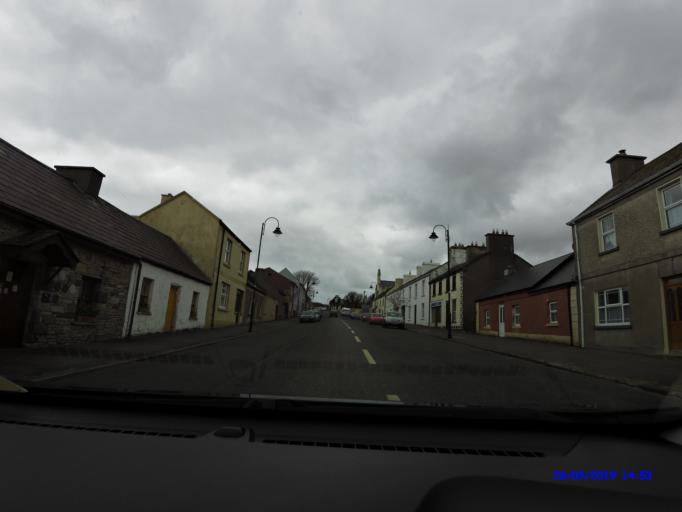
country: IE
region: Connaught
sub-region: Maigh Eo
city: Crossmolina
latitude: 54.2798
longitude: -9.3730
